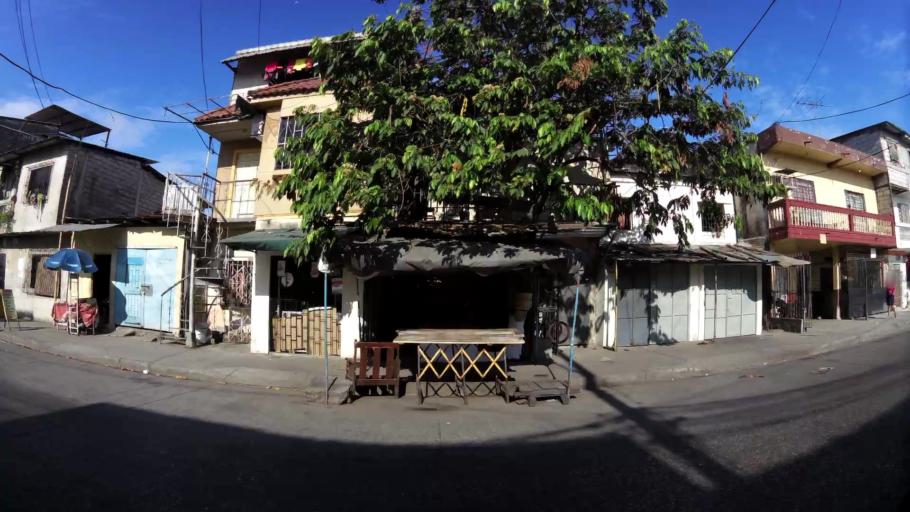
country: EC
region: Guayas
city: Guayaquil
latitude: -2.2267
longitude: -79.9296
